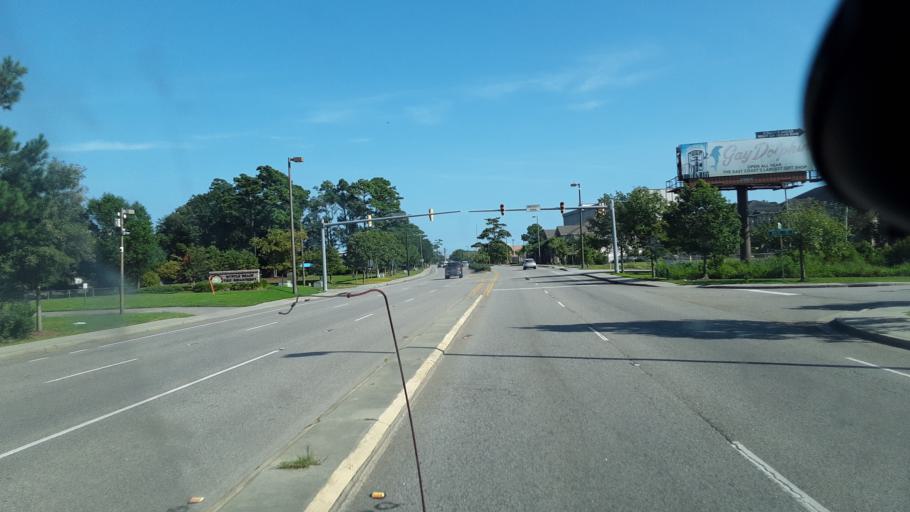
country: US
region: South Carolina
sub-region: Horry County
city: Myrtle Beach
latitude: 33.7011
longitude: -78.8875
